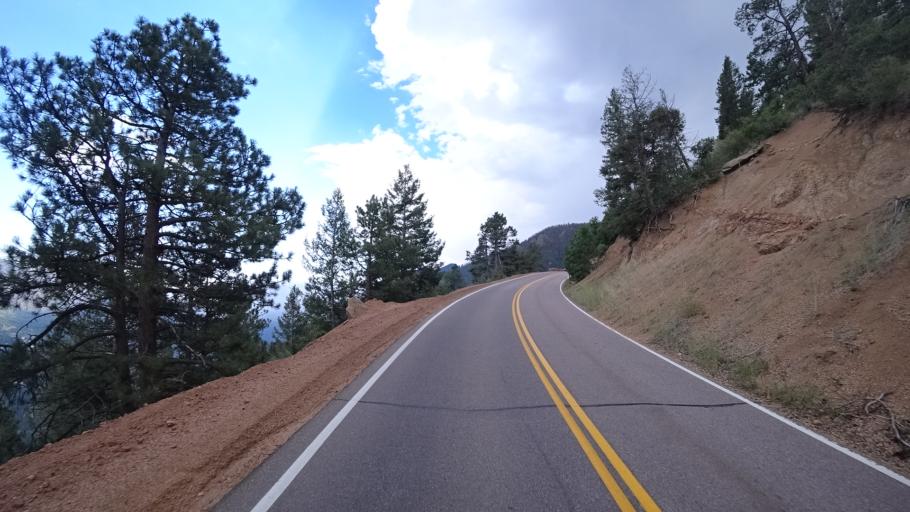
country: US
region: Colorado
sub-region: El Paso County
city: Cascade-Chipita Park
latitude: 38.9000
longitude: -104.9798
